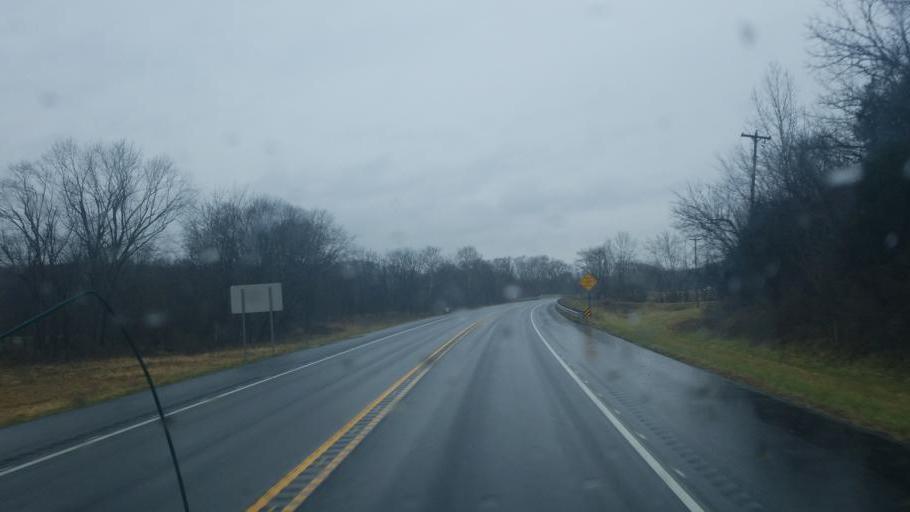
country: US
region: Indiana
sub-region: Brown County
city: Nashville
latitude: 39.1911
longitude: -86.1937
